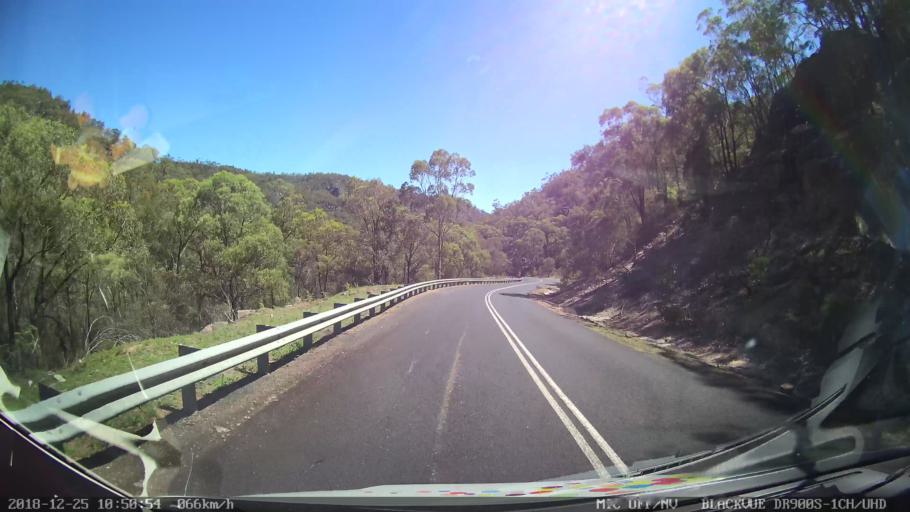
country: AU
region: New South Wales
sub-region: Upper Hunter Shire
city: Merriwa
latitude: -32.4418
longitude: 150.2685
